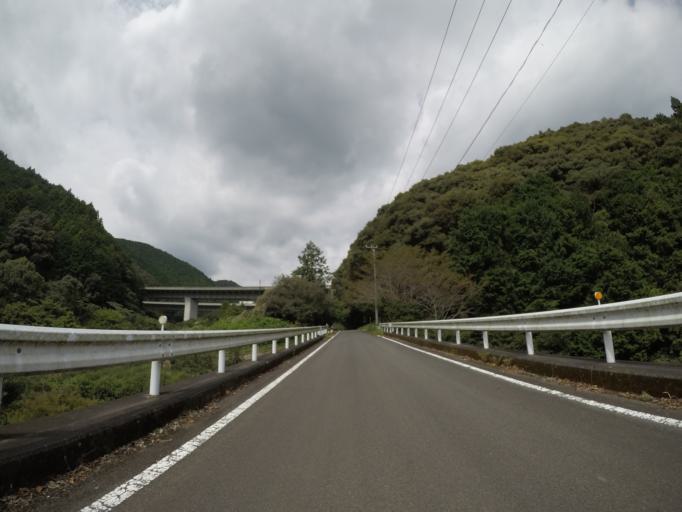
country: JP
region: Shizuoka
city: Shimada
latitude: 34.8741
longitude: 138.1785
